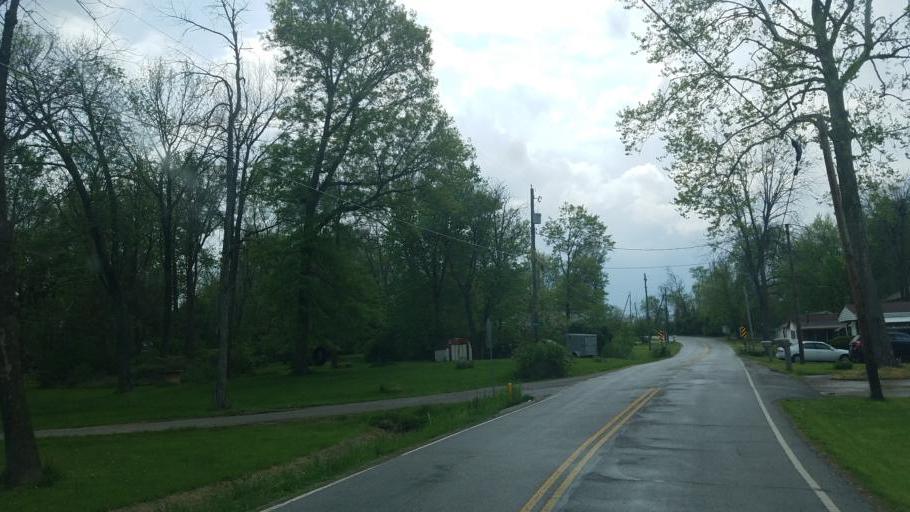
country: US
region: Ohio
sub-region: Fairfield County
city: Fairfield Beach
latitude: 39.9181
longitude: -82.4843
